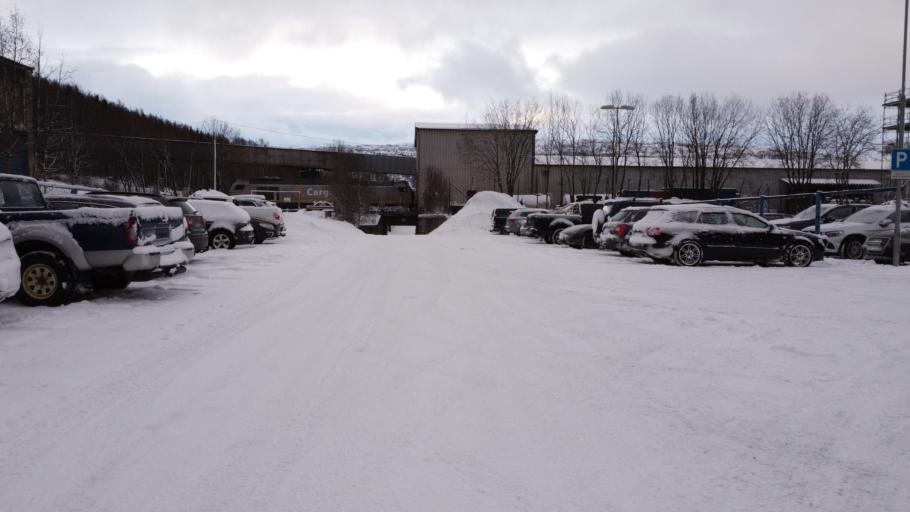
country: NO
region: Nordland
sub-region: Rana
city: Mo i Rana
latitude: 66.3266
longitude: 14.1520
